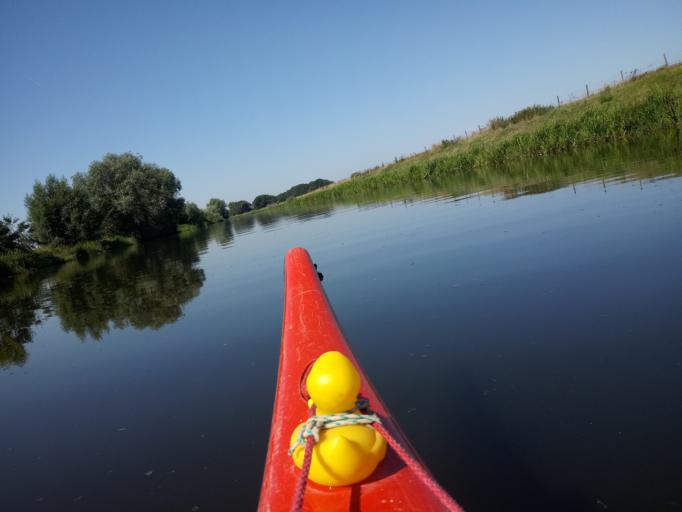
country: NL
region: Gelderland
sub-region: Berkelland
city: Eibergen
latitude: 52.1062
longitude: 6.6854
